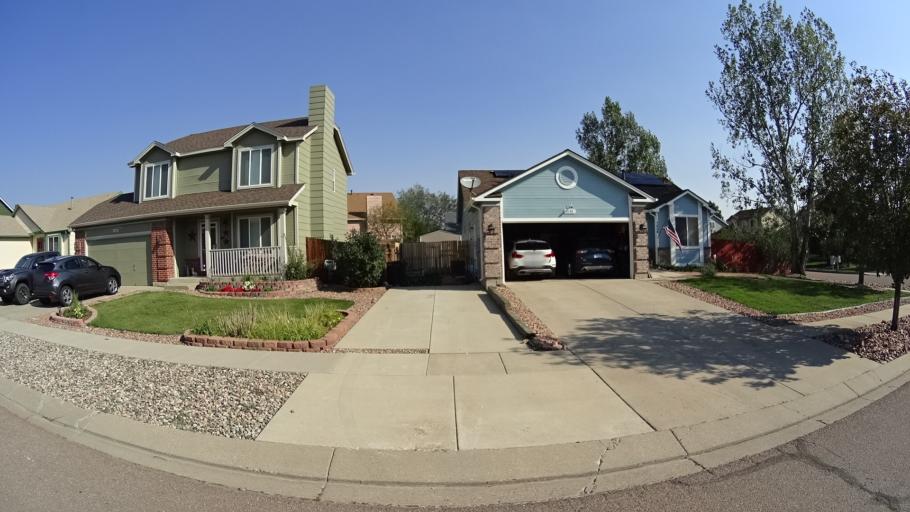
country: US
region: Colorado
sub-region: El Paso County
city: Stratmoor
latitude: 38.7702
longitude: -104.7996
